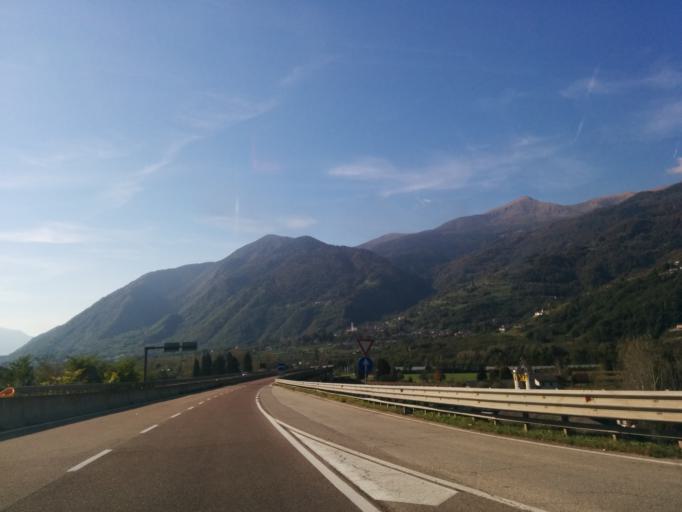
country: IT
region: Trentino-Alto Adige
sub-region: Provincia di Trento
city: Borgo
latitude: 46.0461
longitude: 11.4370
